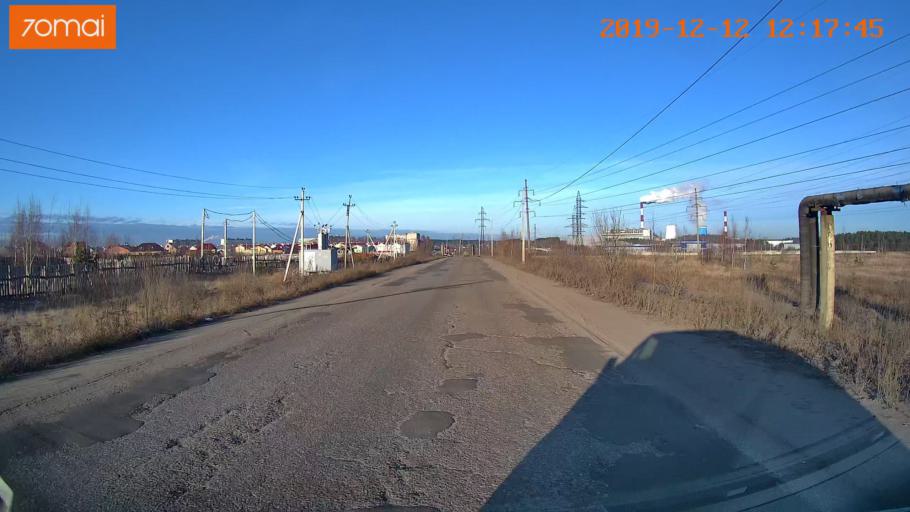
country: RU
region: Ivanovo
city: Kokhma
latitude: 56.9460
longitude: 41.1119
